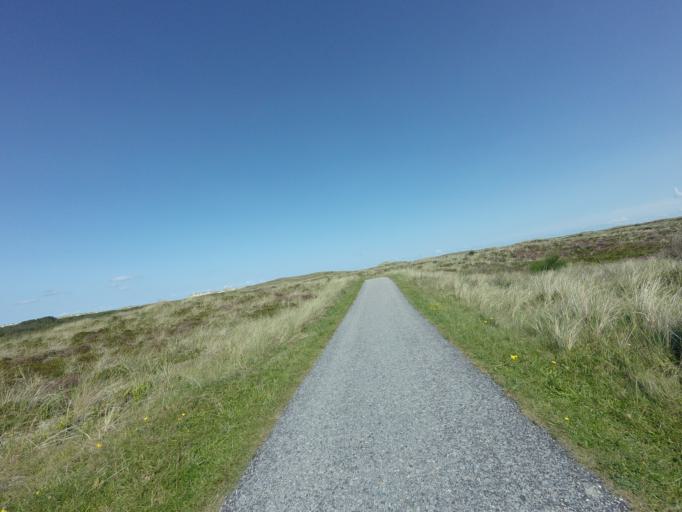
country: NL
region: Friesland
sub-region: Gemeente Terschelling
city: West-Terschelling
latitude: 53.4139
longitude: 5.3820
